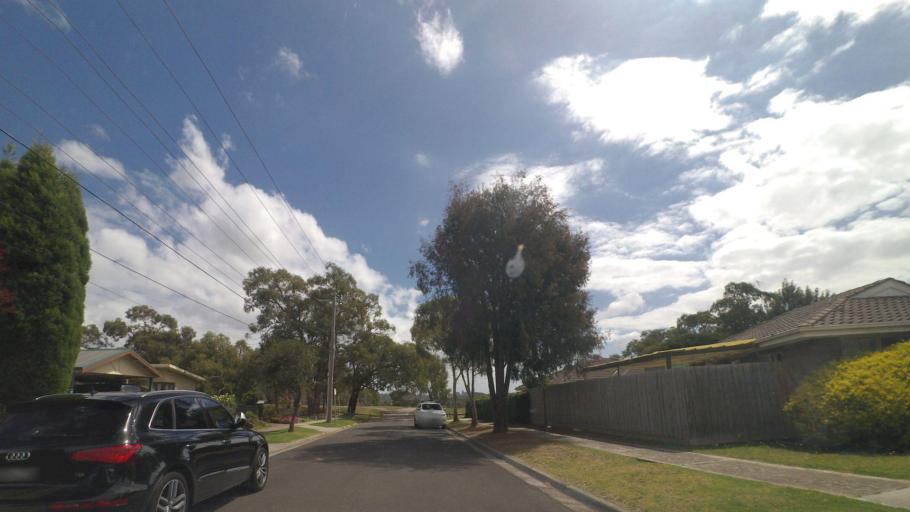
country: AU
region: Victoria
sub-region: Knox
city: Wantirna South
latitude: -37.8845
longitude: 145.2207
